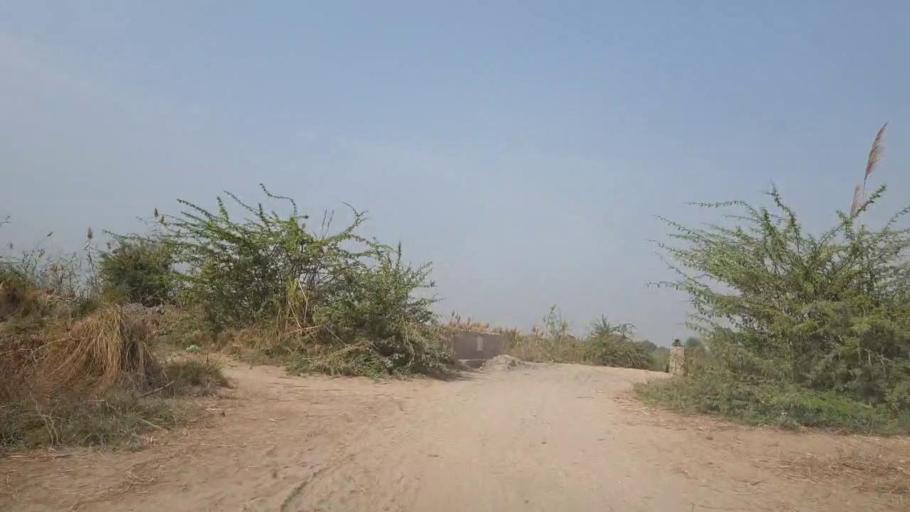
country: PK
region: Sindh
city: Mirpur Khas
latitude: 25.5749
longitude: 69.1357
